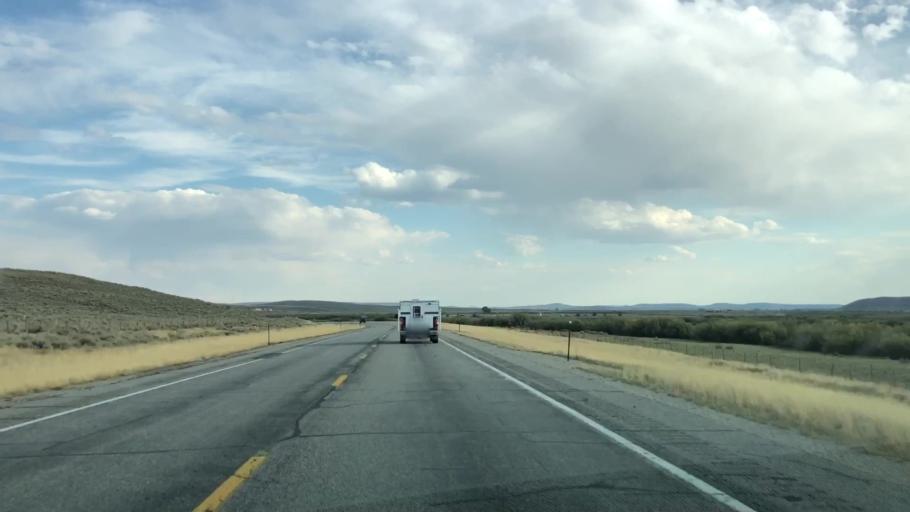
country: US
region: Wyoming
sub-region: Sublette County
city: Pinedale
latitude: 43.0243
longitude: -110.1238
